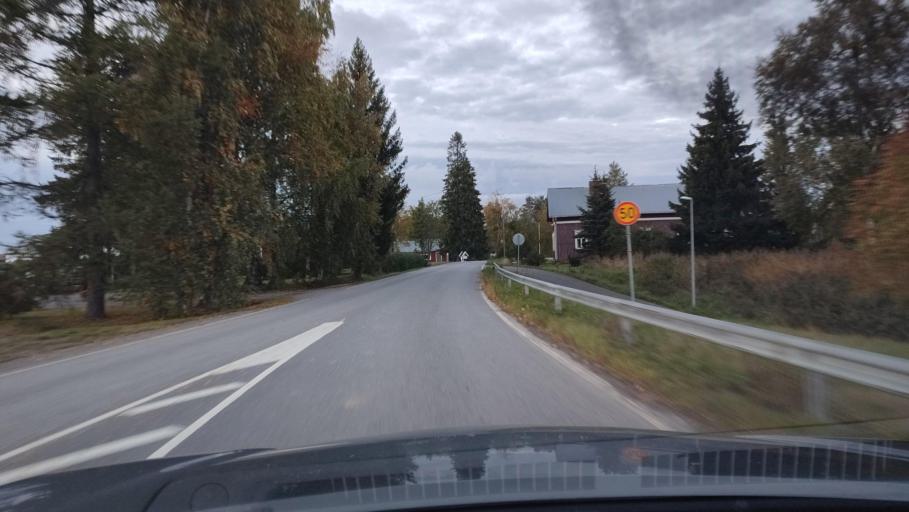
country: FI
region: Ostrobothnia
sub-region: Sydosterbotten
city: Kristinestad
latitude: 62.2608
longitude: 21.5081
